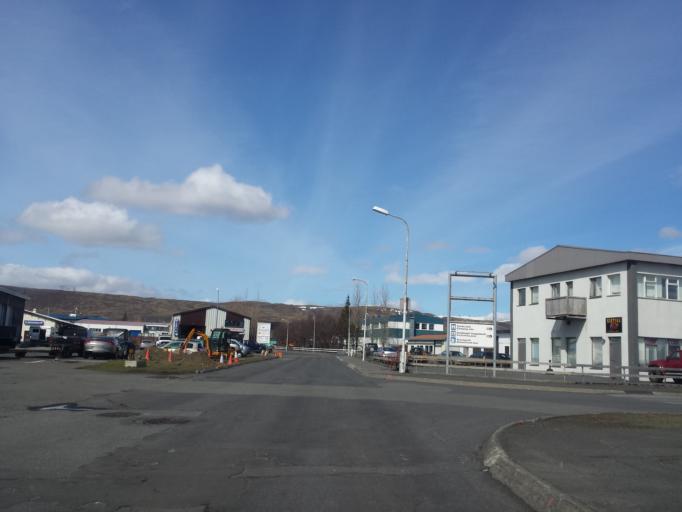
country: IS
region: South
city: Hveragerdi
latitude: 63.9961
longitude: -21.1858
